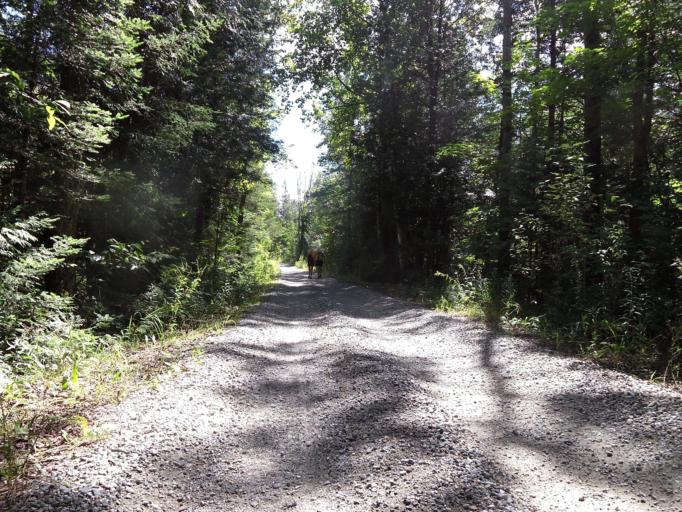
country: CA
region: Ontario
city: Renfrew
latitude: 45.0216
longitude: -76.7041
